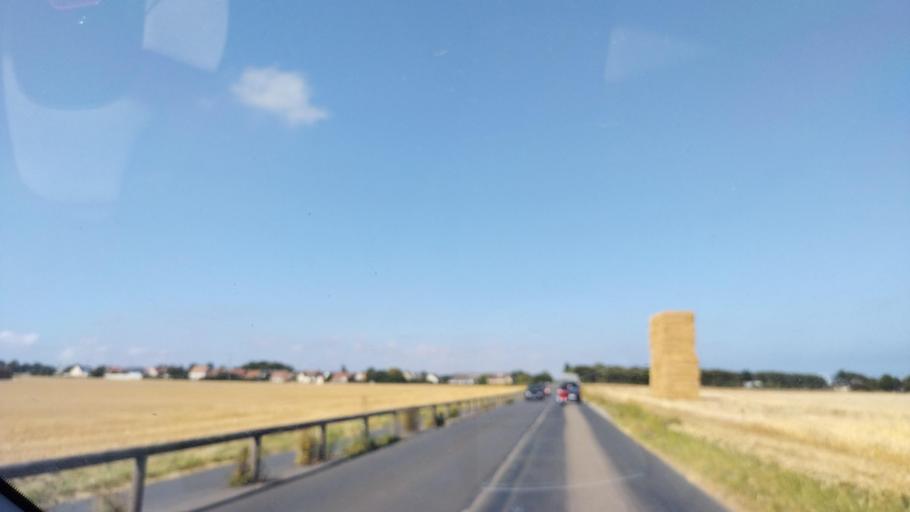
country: FR
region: Lower Normandy
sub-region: Departement du Calvados
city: Bernieres-sur-Mer
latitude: 49.3295
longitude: -0.4355
